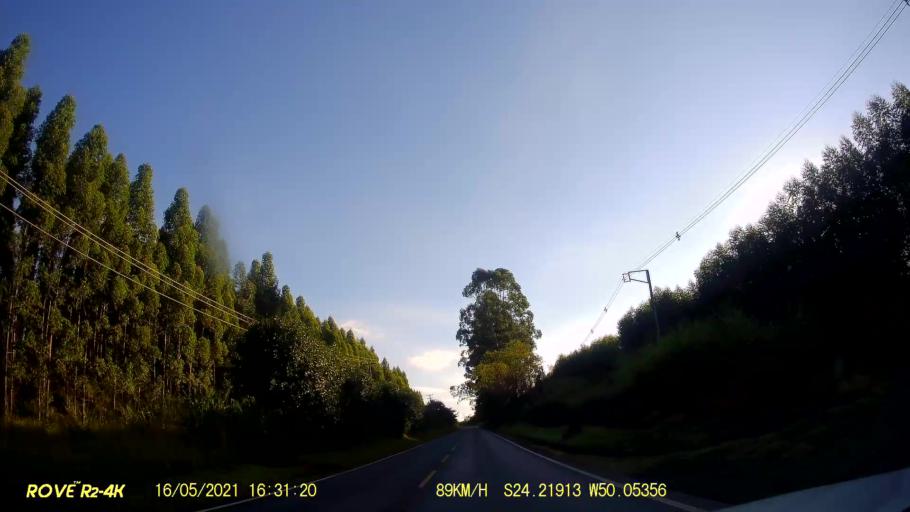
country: BR
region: Parana
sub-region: Pirai Do Sul
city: Pirai do Sul
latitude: -24.2192
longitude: -50.0538
